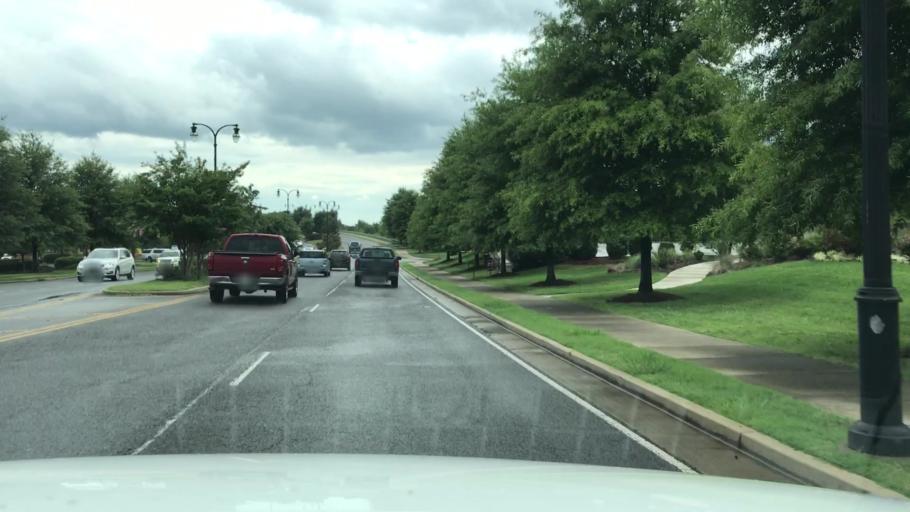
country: US
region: Tennessee
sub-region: Sumner County
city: Hendersonville
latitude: 36.3269
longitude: -86.5951
